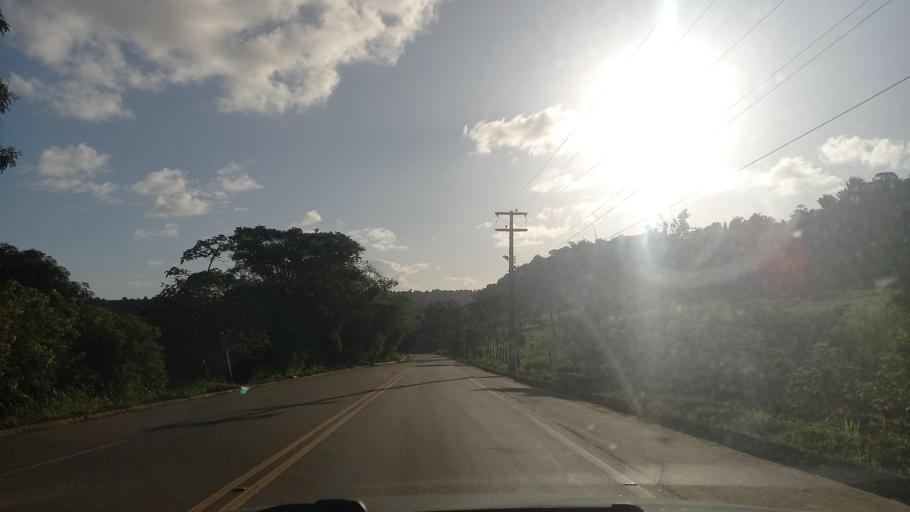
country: BR
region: Alagoas
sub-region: Sao Miguel Dos Campos
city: Sao Miguel dos Campos
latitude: -9.8090
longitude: -36.2162
